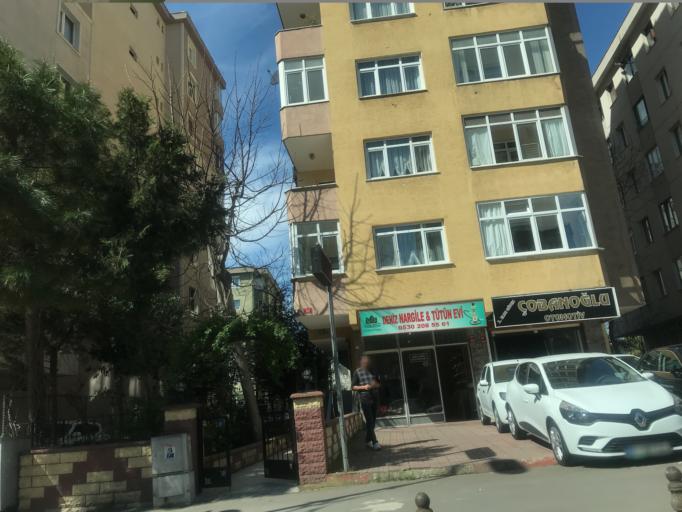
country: TR
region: Istanbul
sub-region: Atasehir
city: Atasehir
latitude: 40.9768
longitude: 29.1131
